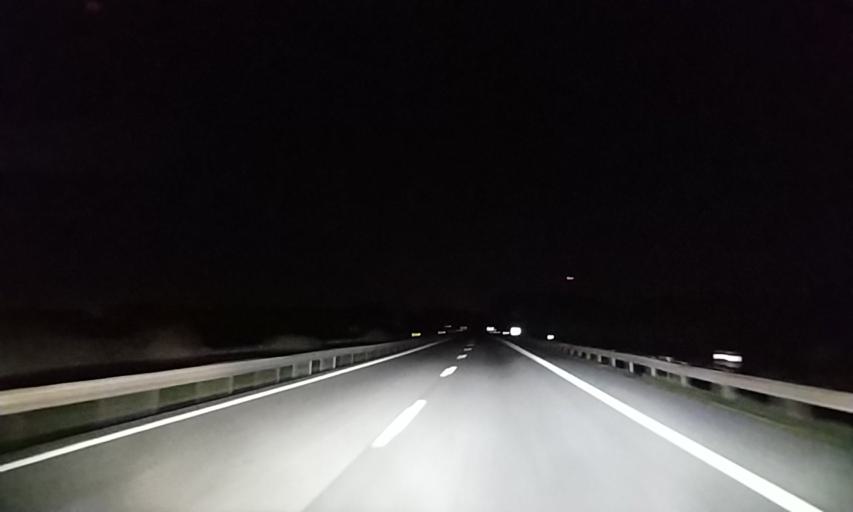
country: PT
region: Aveiro
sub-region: Estarreja
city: Salreu
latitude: 40.7117
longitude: -8.5217
